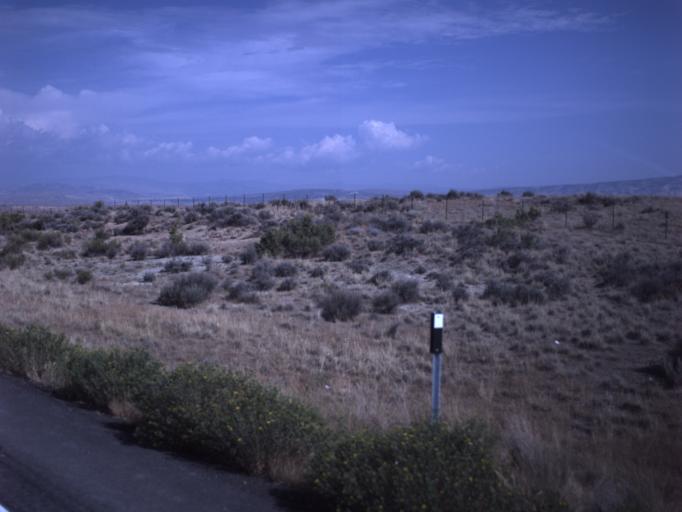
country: US
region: Utah
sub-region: Uintah County
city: Naples
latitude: 40.3342
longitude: -109.2865
